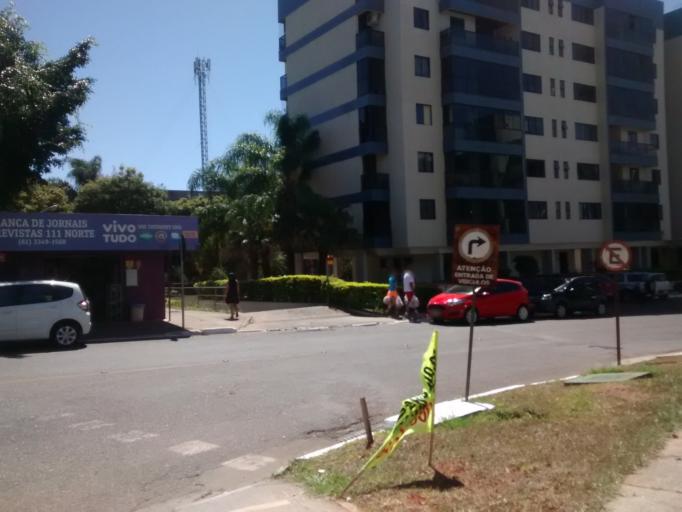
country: BR
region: Federal District
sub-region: Brasilia
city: Brasilia
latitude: -15.7539
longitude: -47.8902
